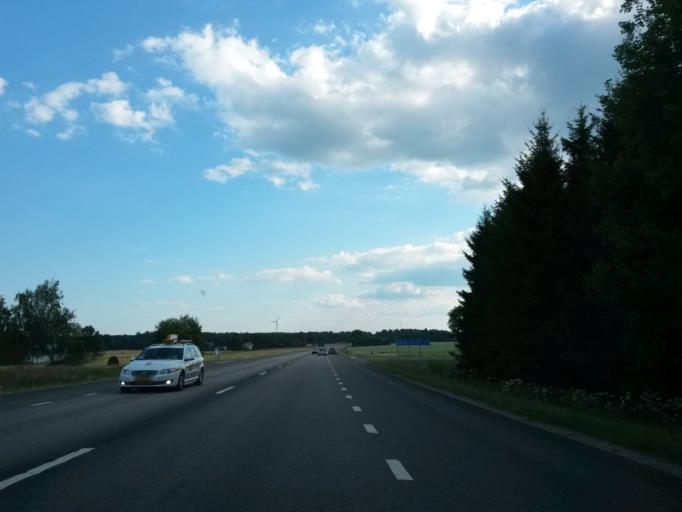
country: SE
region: Vaestra Goetaland
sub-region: Vargarda Kommun
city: Vargarda
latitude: 58.1390
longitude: 12.8620
